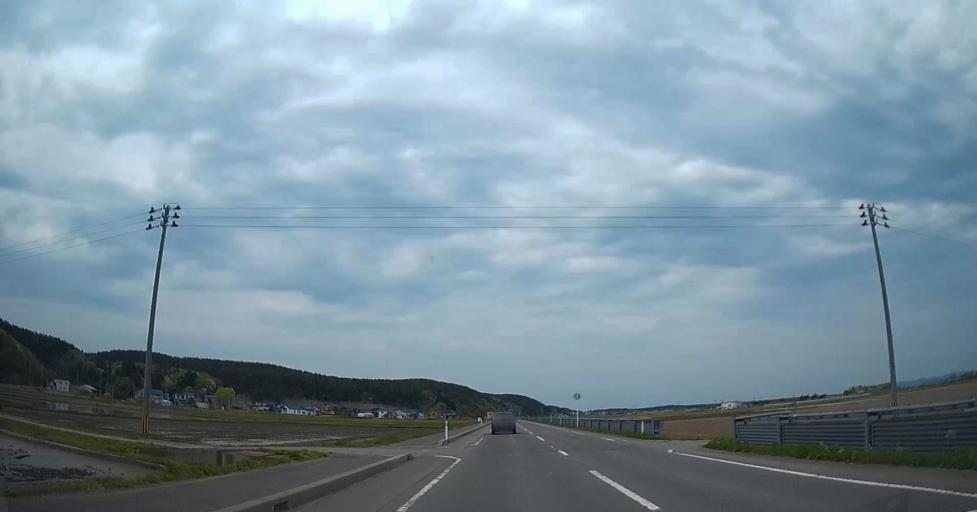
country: JP
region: Aomori
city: Shimokizukuri
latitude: 40.9930
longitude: 140.3619
